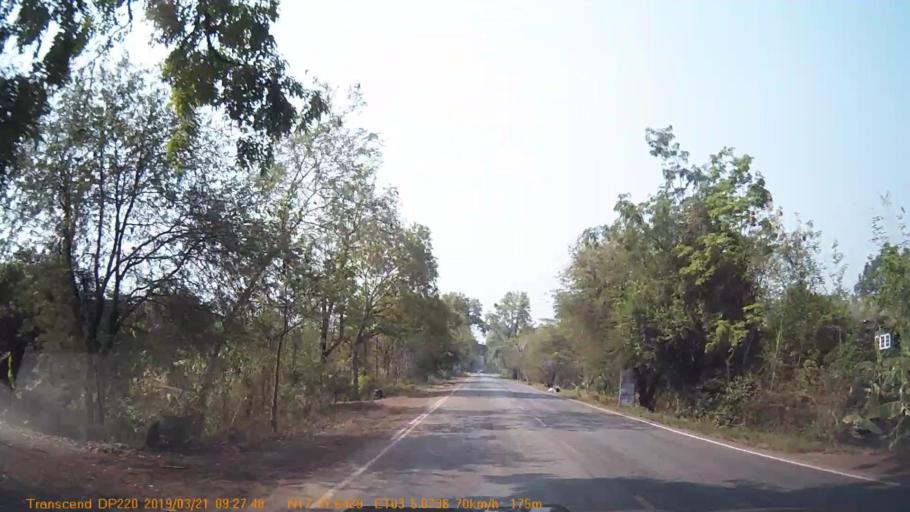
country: TH
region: Changwat Udon Thani
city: Phibun Rak
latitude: 17.6271
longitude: 103.0845
